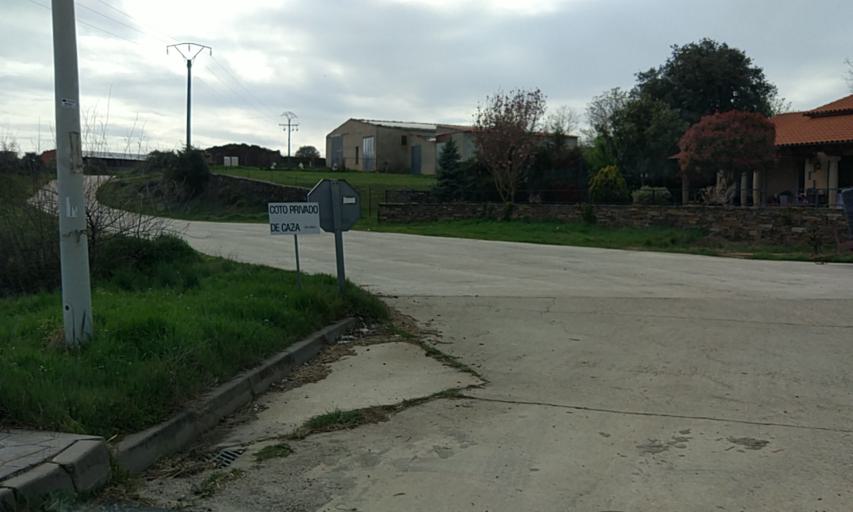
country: ES
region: Castille and Leon
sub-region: Provincia de Salamanca
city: Robleda
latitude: 40.3865
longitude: -6.6086
